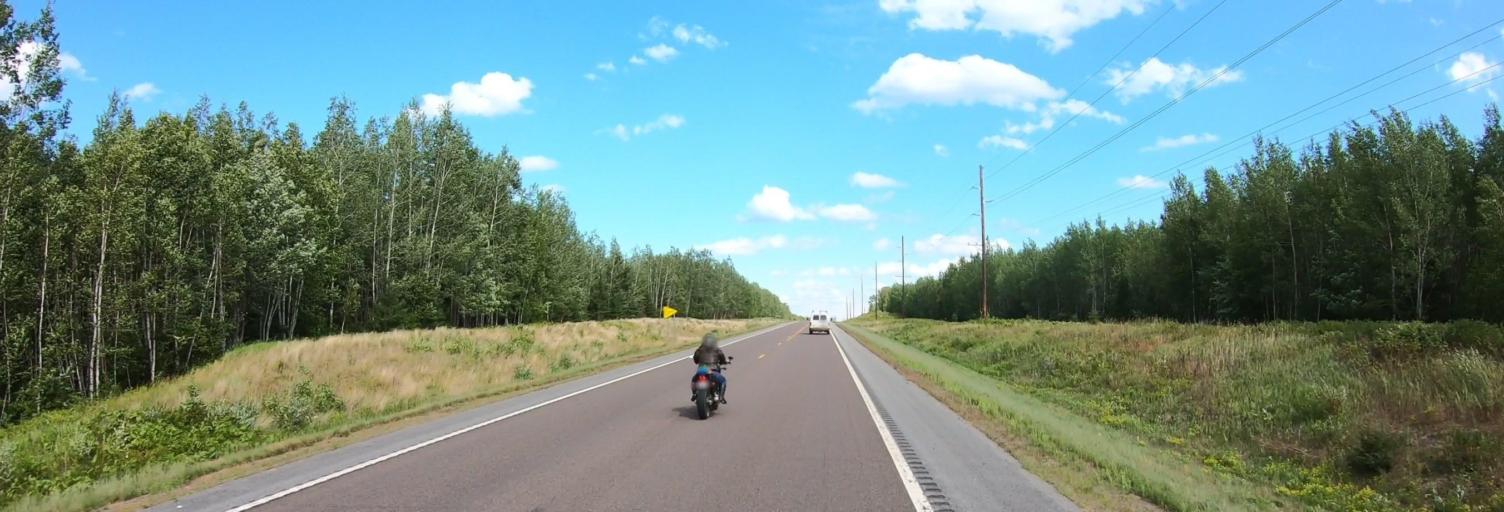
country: US
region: Minnesota
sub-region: Saint Louis County
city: Virginia
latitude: 47.8587
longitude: -92.4434
